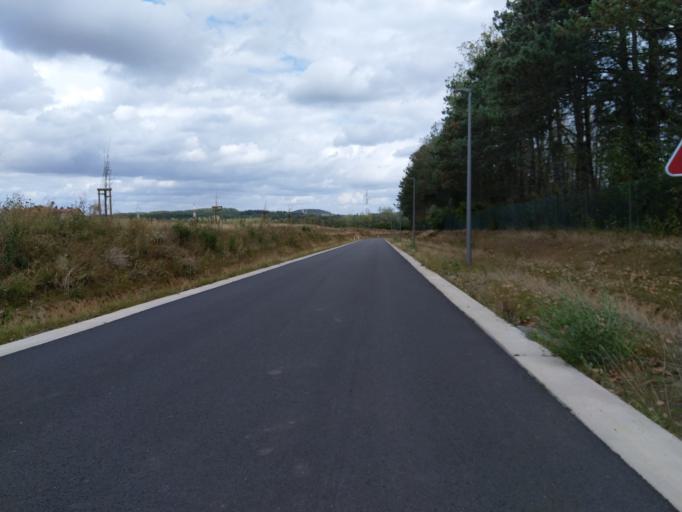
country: BE
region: Wallonia
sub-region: Province du Hainaut
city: Courcelles
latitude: 50.3965
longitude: 4.3481
